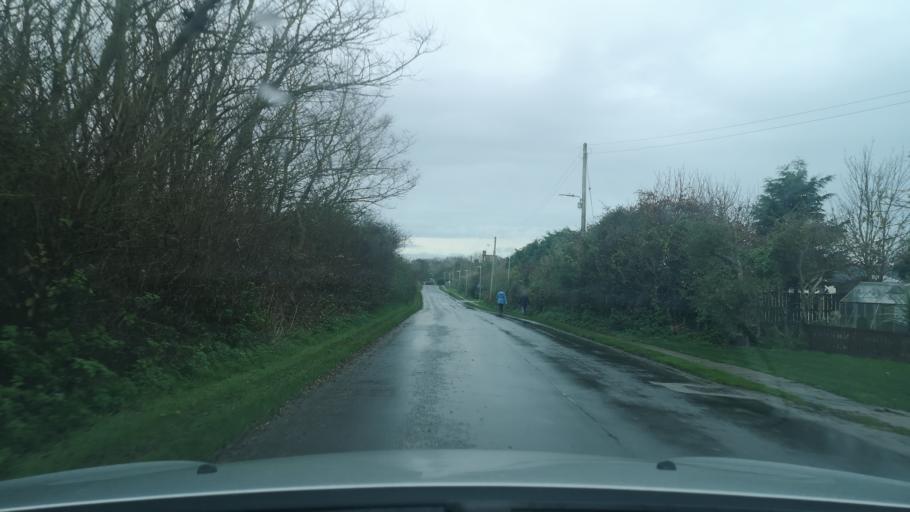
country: GB
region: England
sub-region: East Riding of Yorkshire
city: Easington
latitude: 53.6484
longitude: 0.1231
